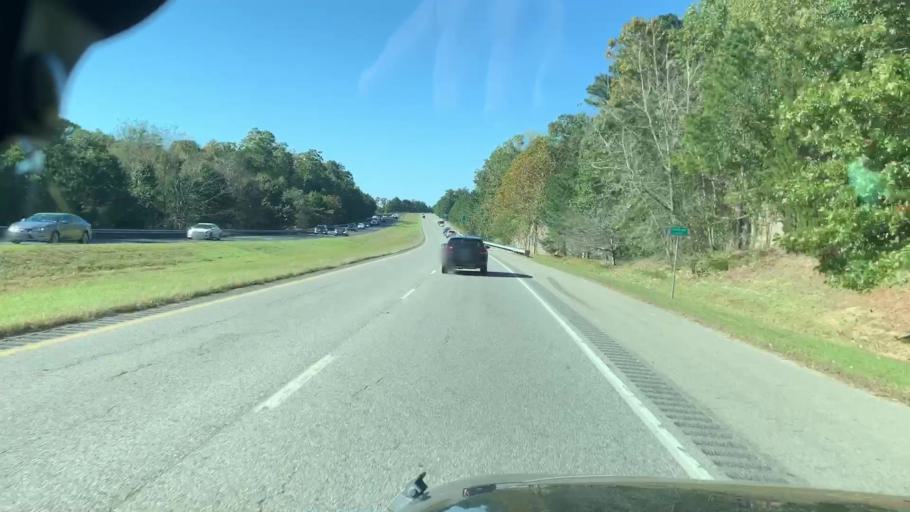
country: US
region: Virginia
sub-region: James City County
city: Williamsburg
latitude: 37.2681
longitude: -76.7454
